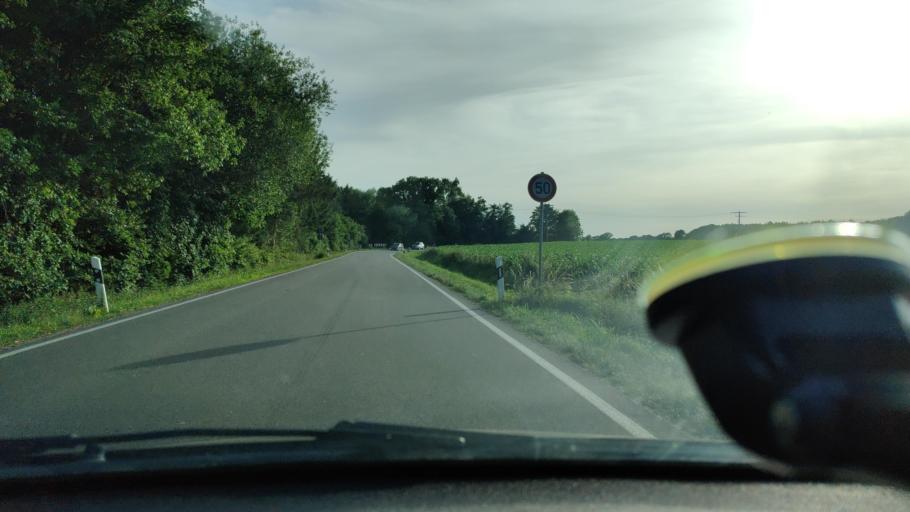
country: DE
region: North Rhine-Westphalia
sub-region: Regierungsbezirk Munster
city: Billerbeck
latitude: 51.9895
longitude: 7.2536
